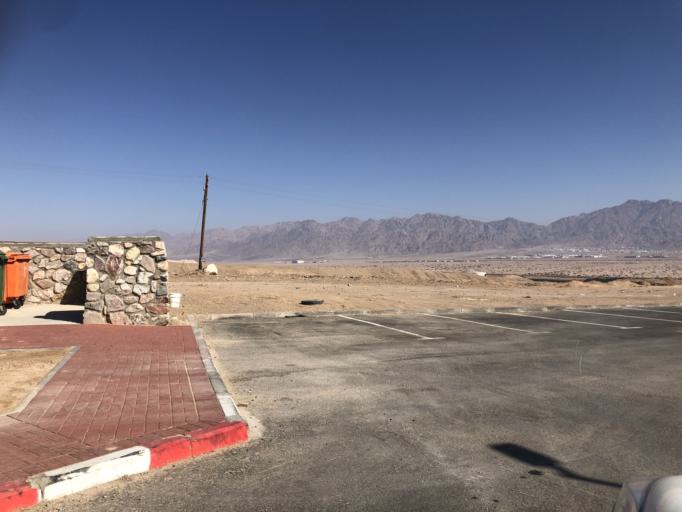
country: IL
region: Southern District
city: Eilat
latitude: 29.5835
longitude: 34.9610
